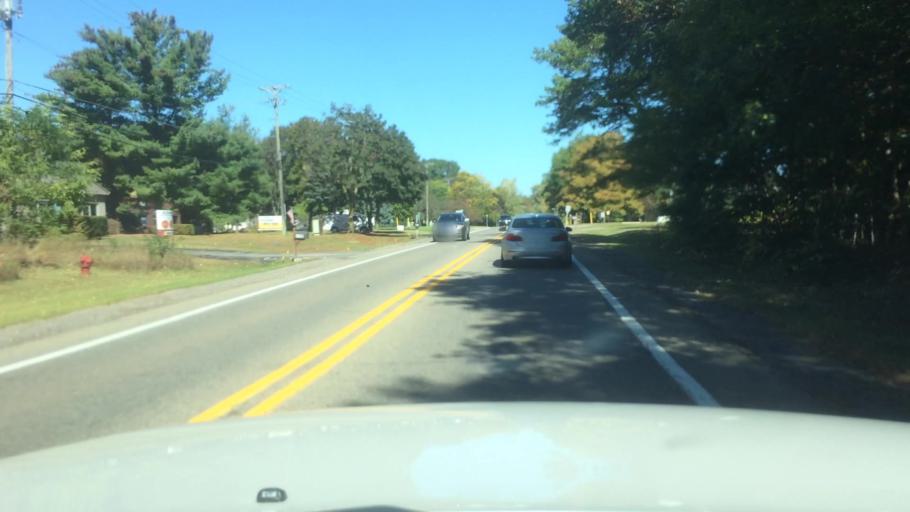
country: US
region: Michigan
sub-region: Oakland County
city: Wolverine Lake
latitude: 42.5739
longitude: -83.4500
